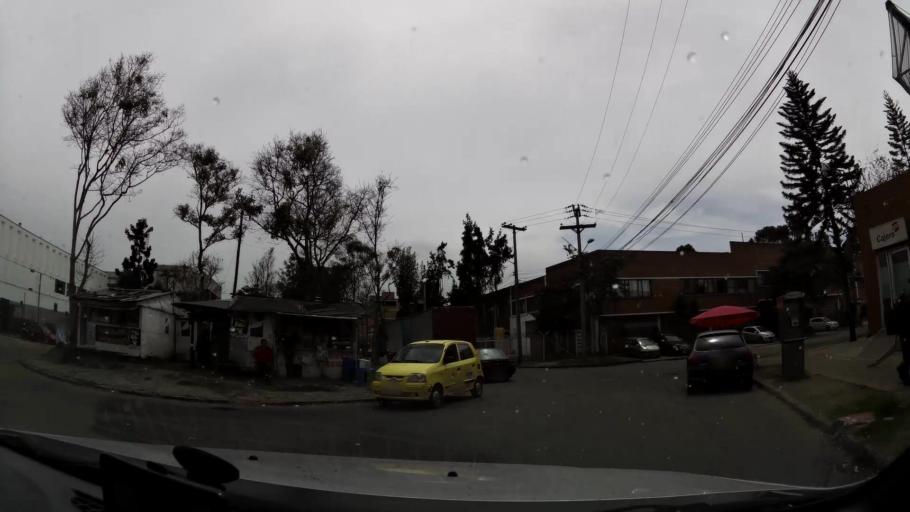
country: CO
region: Bogota D.C.
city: Bogota
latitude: 4.6378
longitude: -74.1211
